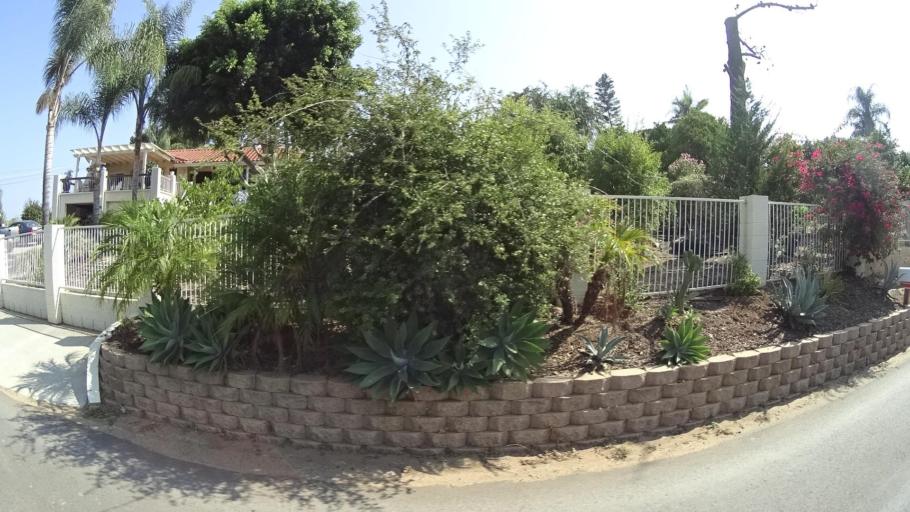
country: US
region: California
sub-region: San Diego County
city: Vista
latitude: 33.2389
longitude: -117.2459
